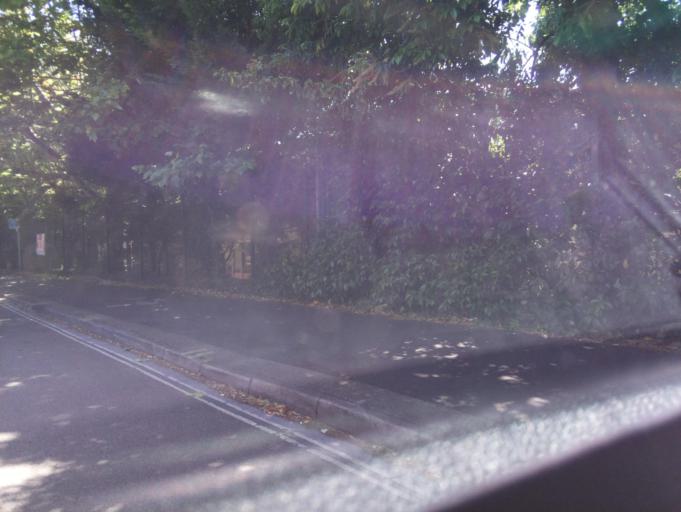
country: GB
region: England
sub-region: Borough of Torbay
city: Torquay
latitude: 50.4675
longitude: -3.5436
